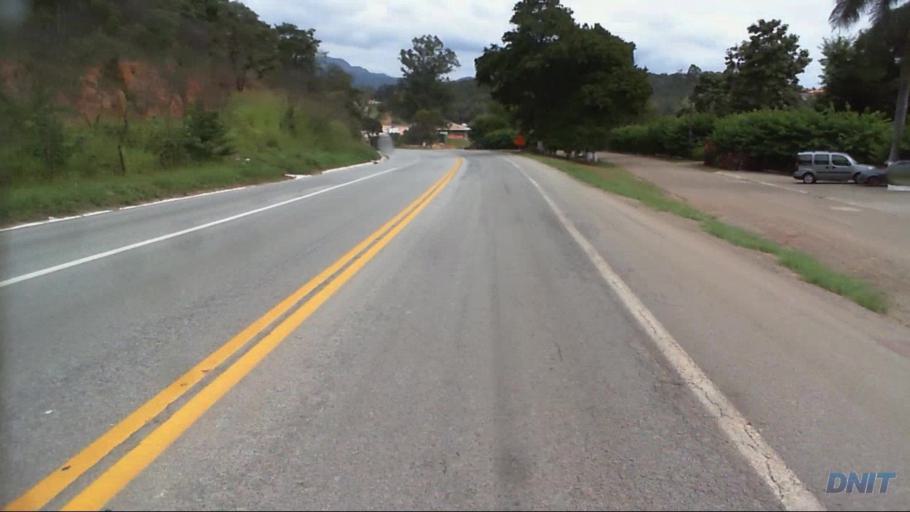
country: BR
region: Minas Gerais
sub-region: Caete
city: Caete
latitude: -19.7658
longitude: -43.6435
